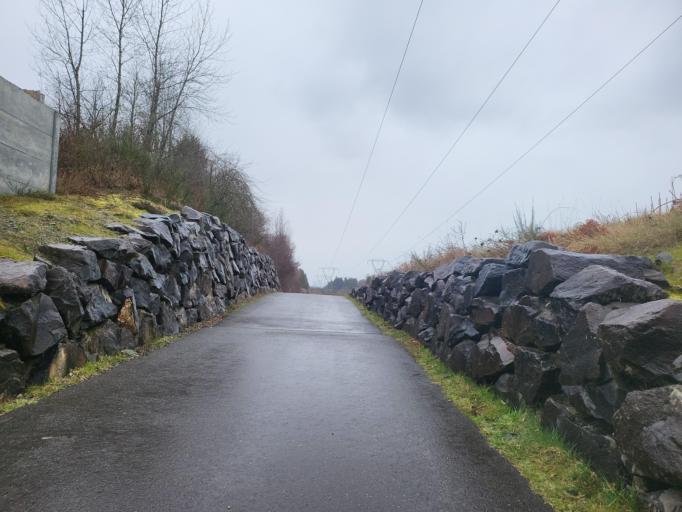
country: US
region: Washington
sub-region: King County
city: East Hill-Meridian
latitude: 47.4249
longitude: -122.1728
